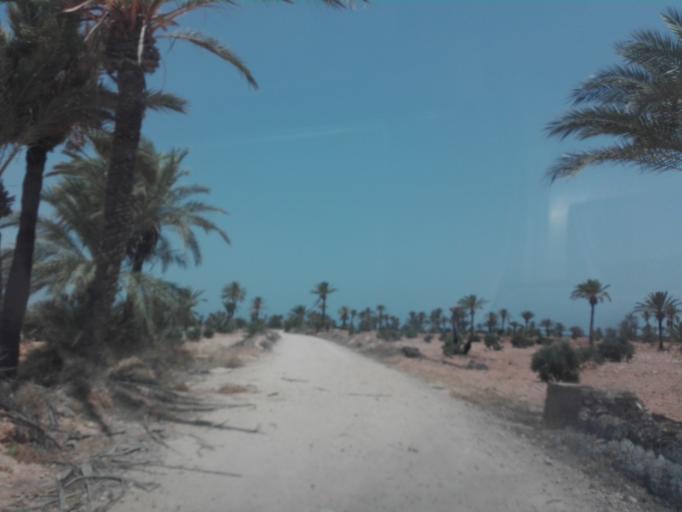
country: TN
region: Safaqis
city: Al Qarmadah
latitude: 34.6642
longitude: 11.0927
